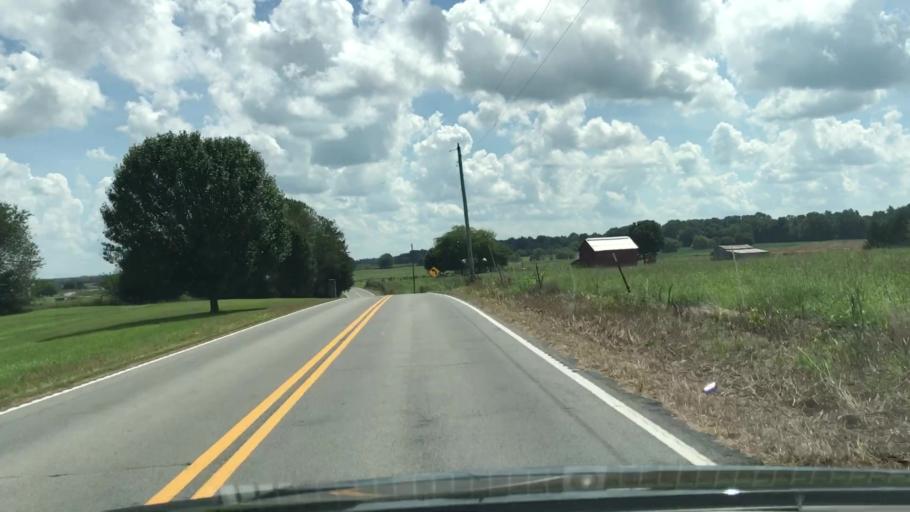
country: US
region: Tennessee
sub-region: Robertson County
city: Springfield
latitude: 36.5873
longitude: -86.8938
